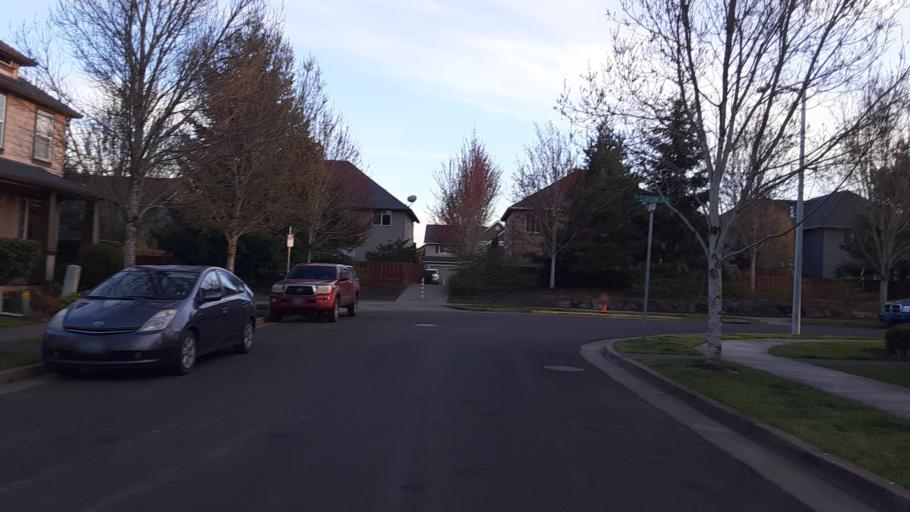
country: US
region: Oregon
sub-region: Benton County
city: Corvallis
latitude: 44.5334
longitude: -123.2544
